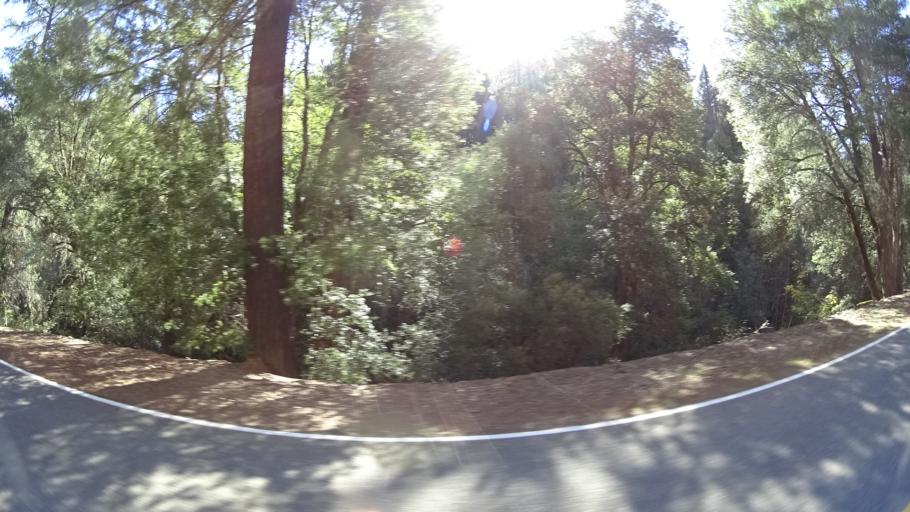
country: US
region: California
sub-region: Trinity County
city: Weaverville
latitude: 41.1718
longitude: -123.0951
